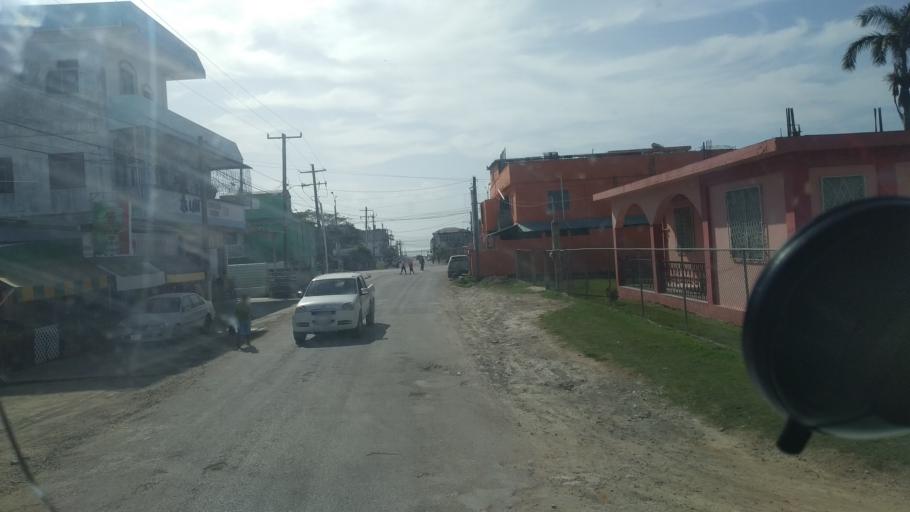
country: BZ
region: Corozal
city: Corozal
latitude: 18.3920
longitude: -88.3903
